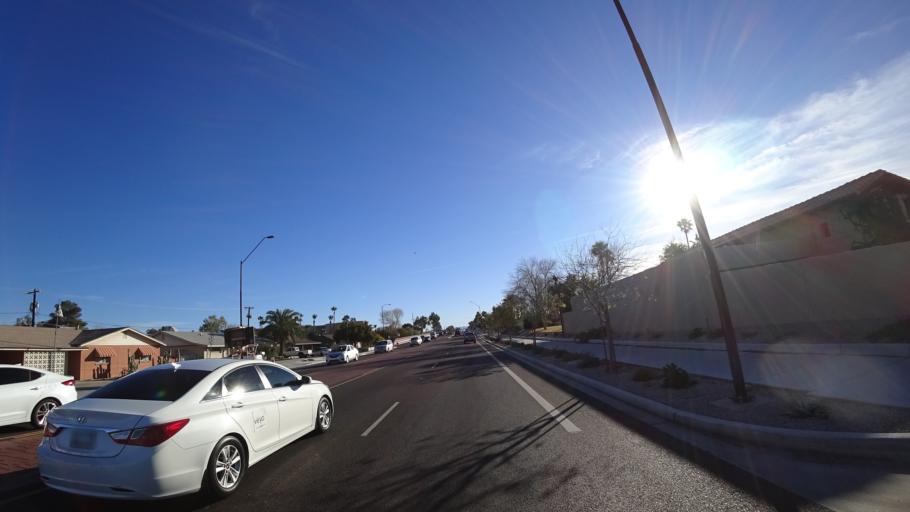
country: US
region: Arizona
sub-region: Maricopa County
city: Scottsdale
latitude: 33.4803
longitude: -111.9145
